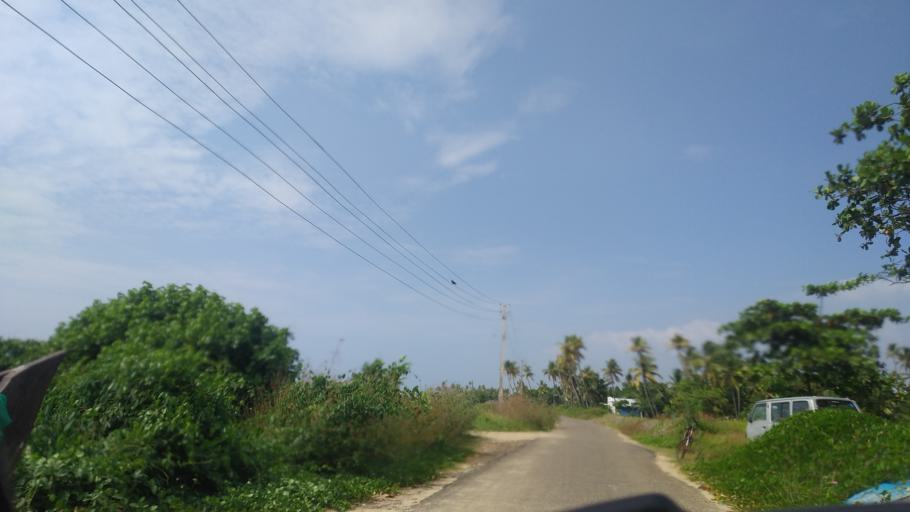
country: IN
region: Kerala
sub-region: Ernakulam
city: Elur
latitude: 10.0478
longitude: 76.2055
